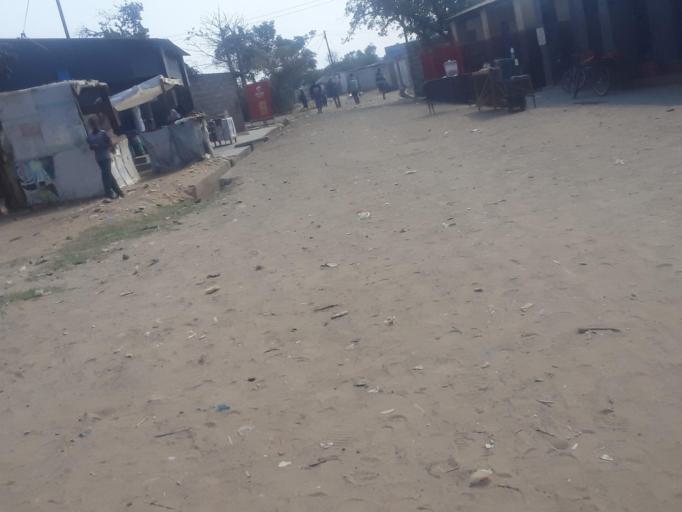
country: ZM
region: Lusaka
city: Lusaka
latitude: -15.3596
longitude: 28.3073
